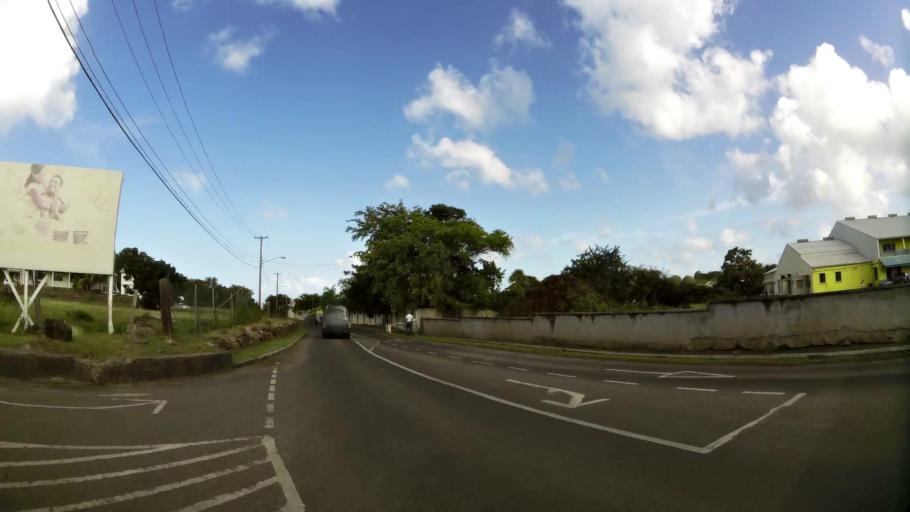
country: KN
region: Saint Paul Charlestown
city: Charlestown
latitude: 17.1315
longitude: -62.6214
